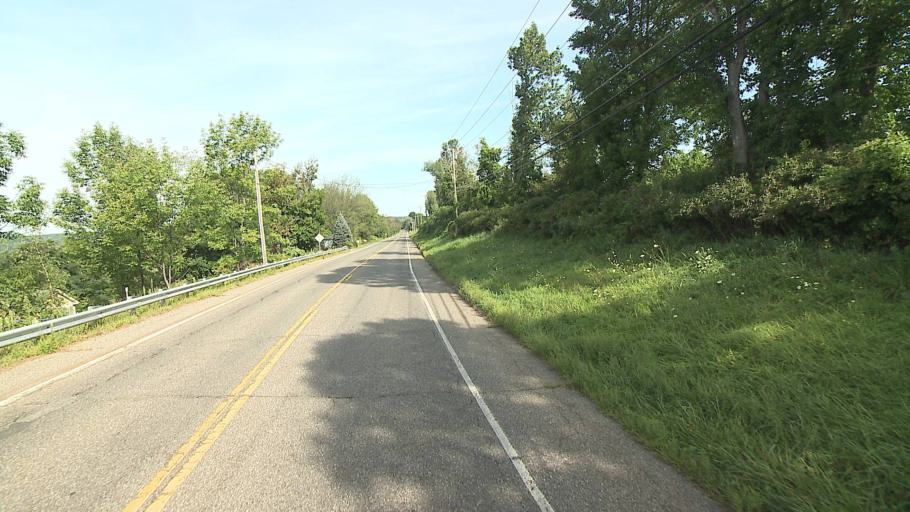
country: US
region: Connecticut
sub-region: Litchfield County
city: Litchfield
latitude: 41.7099
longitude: -73.1361
